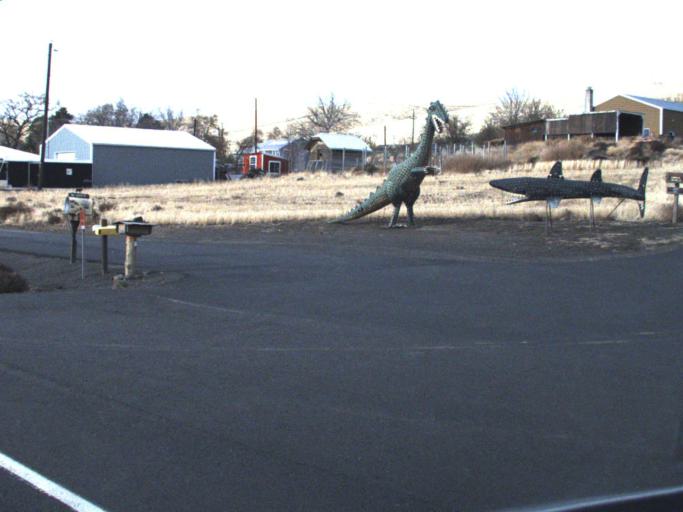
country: US
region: Washington
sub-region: Garfield County
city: Pomeroy
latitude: 46.4730
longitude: -117.5334
